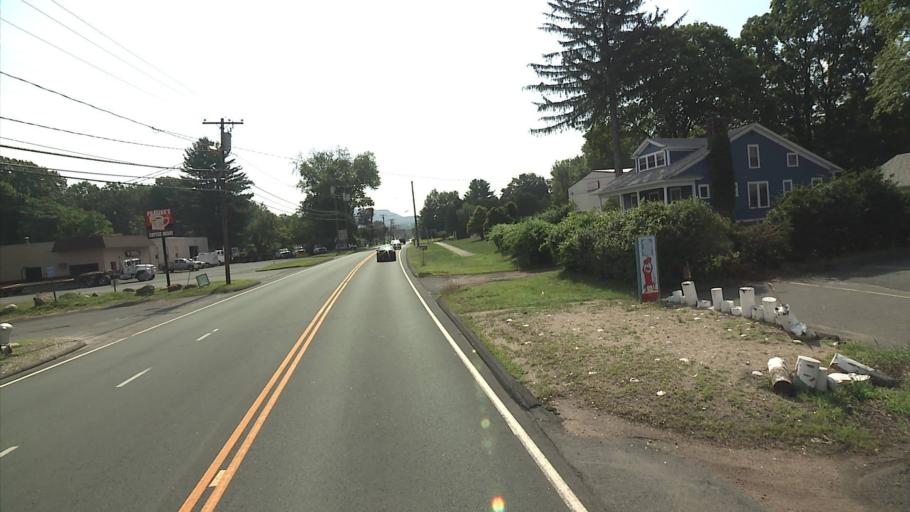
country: US
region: Connecticut
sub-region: New Haven County
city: Cheshire Village
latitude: 41.5647
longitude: -72.8893
